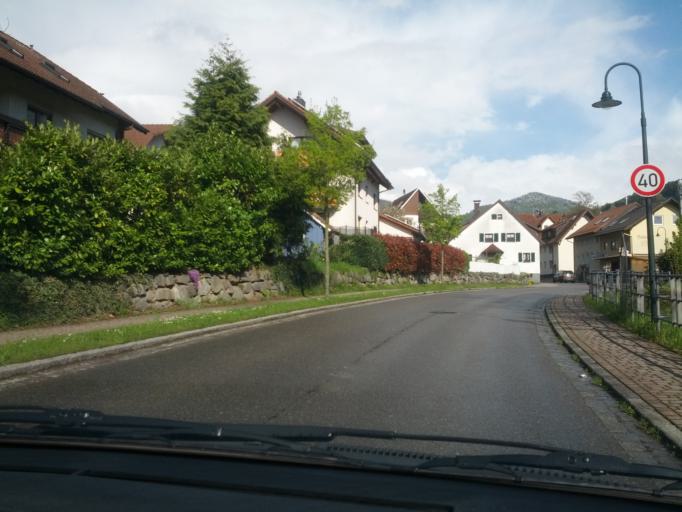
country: DE
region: Baden-Wuerttemberg
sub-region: Freiburg Region
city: Glottertal
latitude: 48.0489
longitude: 7.9528
